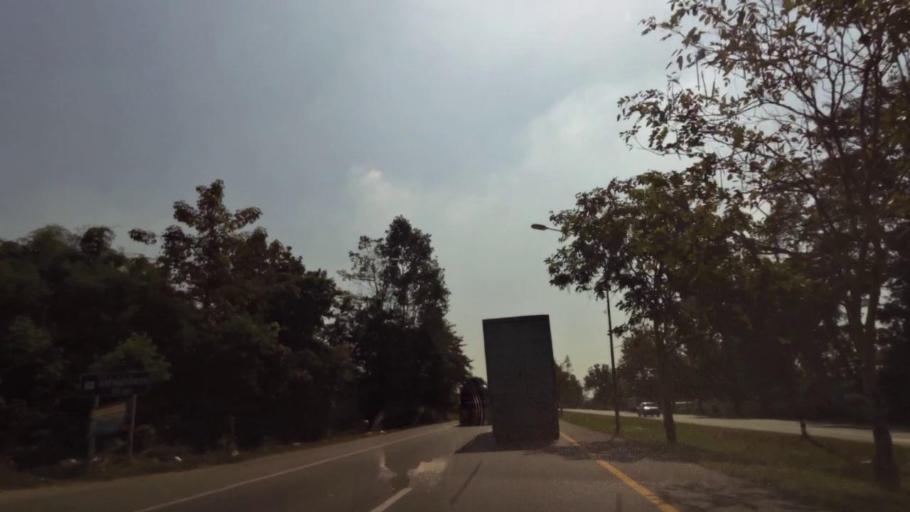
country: TH
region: Phichit
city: Bueng Na Rang
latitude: 16.1381
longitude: 100.1255
